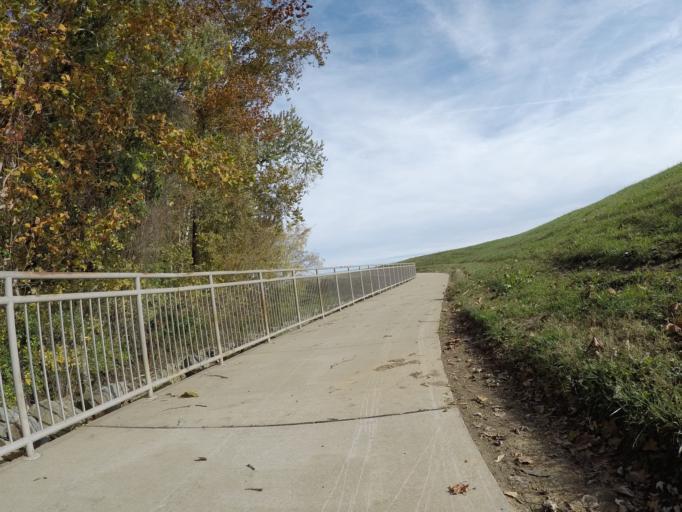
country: US
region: West Virginia
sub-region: Cabell County
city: Huntington
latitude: 38.4163
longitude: -82.4779
